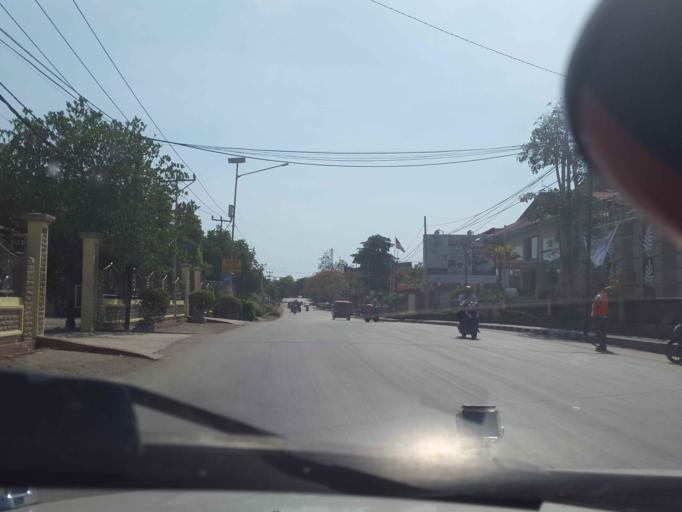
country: ID
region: East Nusa Tenggara
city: Pasirpanjang
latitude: -10.1527
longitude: 123.6009
